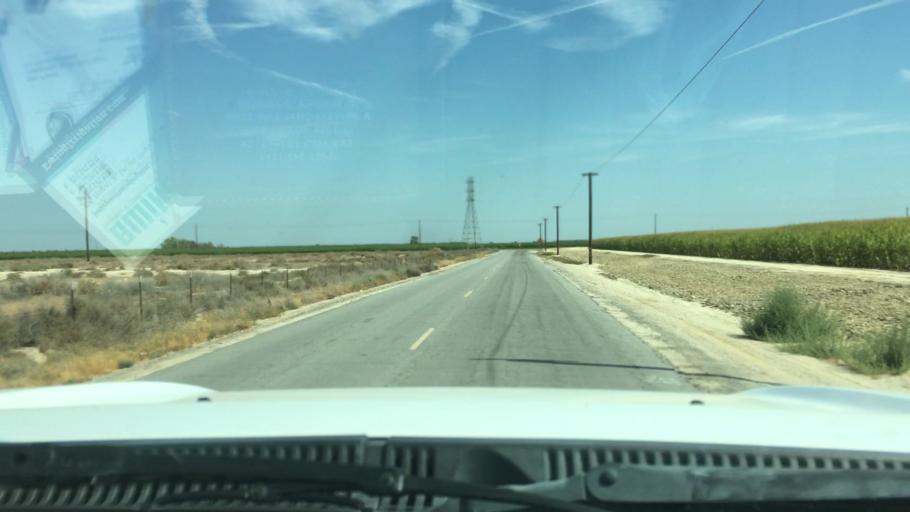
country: US
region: California
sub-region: Kern County
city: Buttonwillow
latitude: 35.4393
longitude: -119.3760
